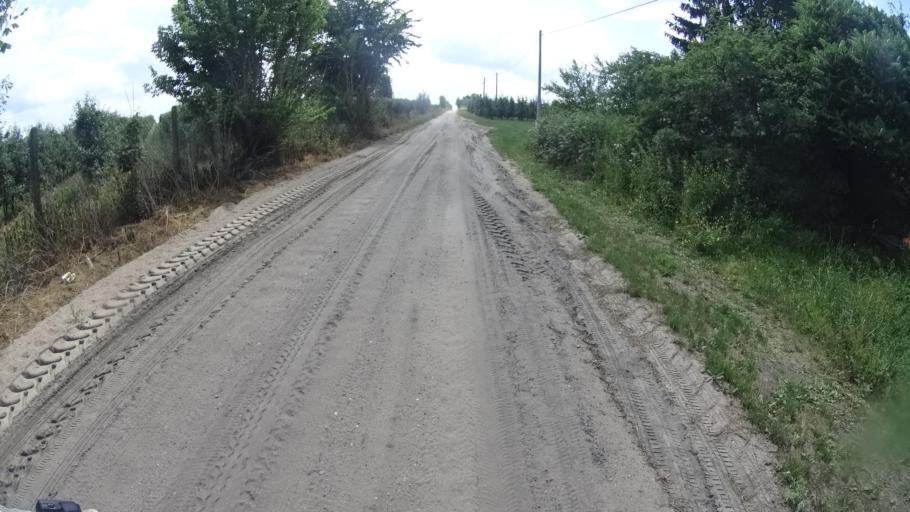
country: PL
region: Masovian Voivodeship
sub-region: Powiat grojecki
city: Goszczyn
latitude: 51.7115
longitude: 20.8313
